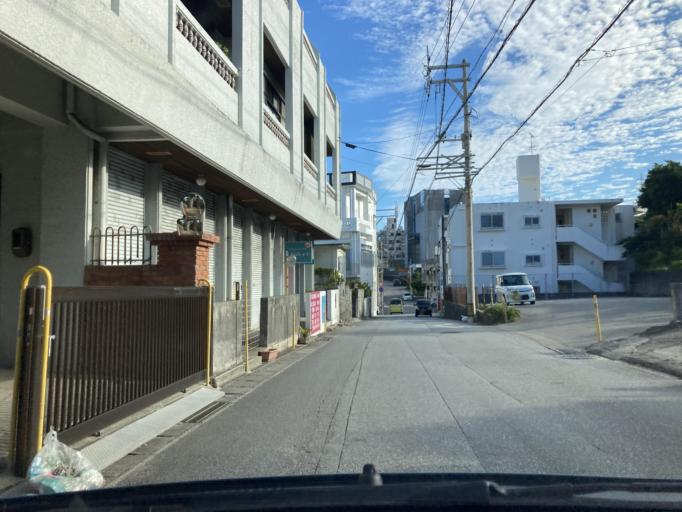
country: JP
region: Okinawa
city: Ginowan
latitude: 26.2766
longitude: 127.7447
